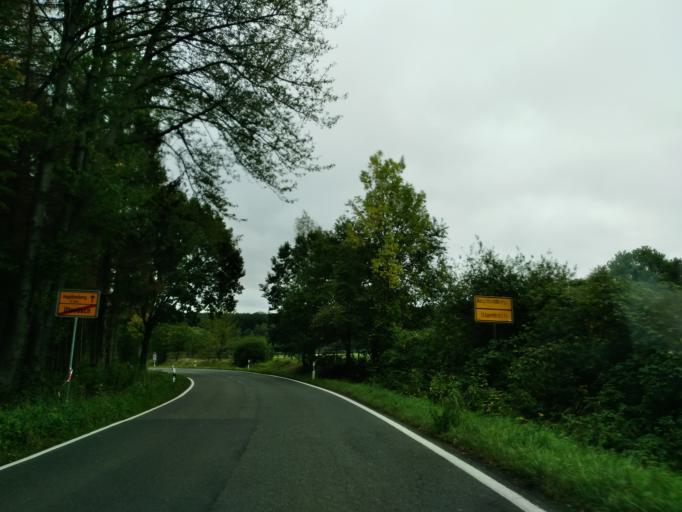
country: DE
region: North Rhine-Westphalia
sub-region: Regierungsbezirk Koln
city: Bad Honnef
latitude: 50.6782
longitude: 7.2718
